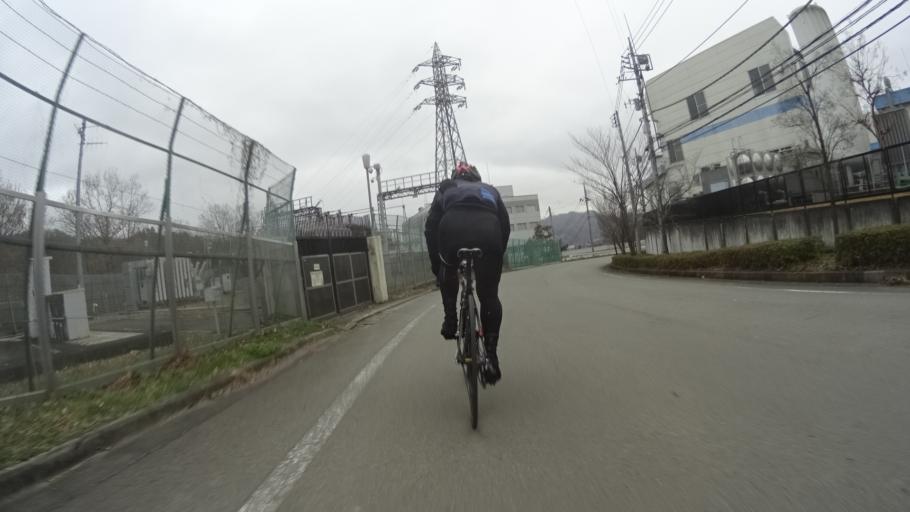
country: JP
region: Yamanashi
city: Uenohara
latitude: 35.6324
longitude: 139.1223
